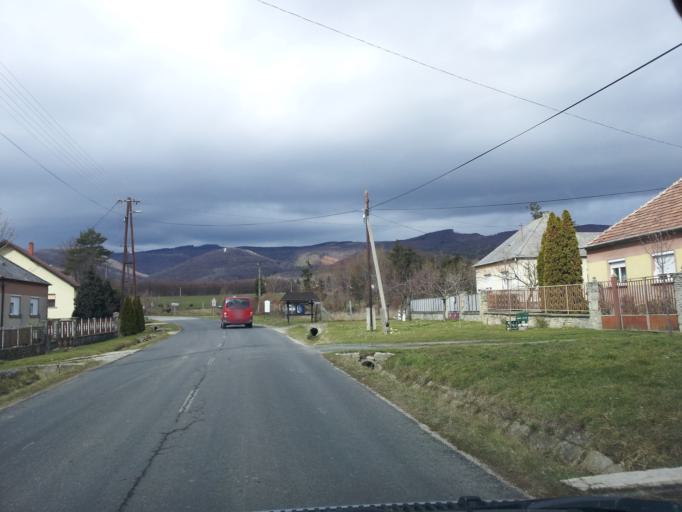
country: HU
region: Vas
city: Koszeg
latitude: 47.3420
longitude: 16.5094
